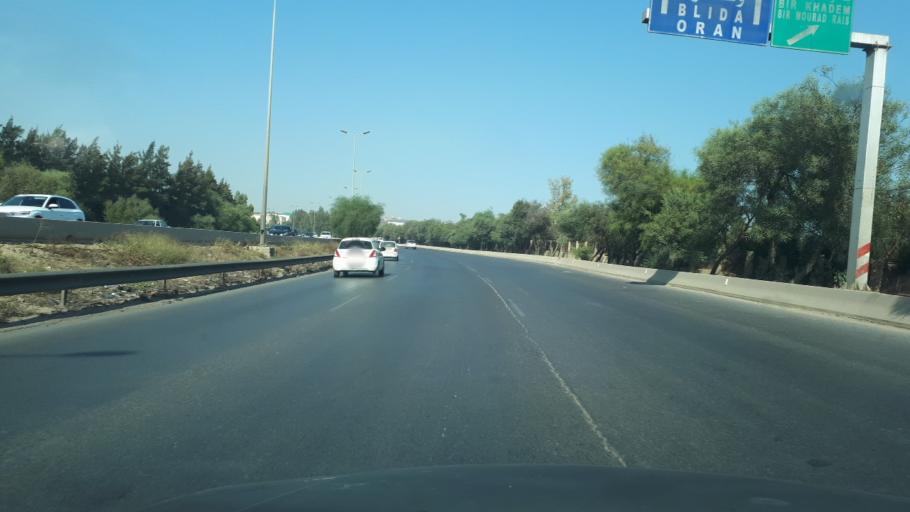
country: DZ
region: Tipaza
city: Baraki
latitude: 36.6788
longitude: 3.0634
